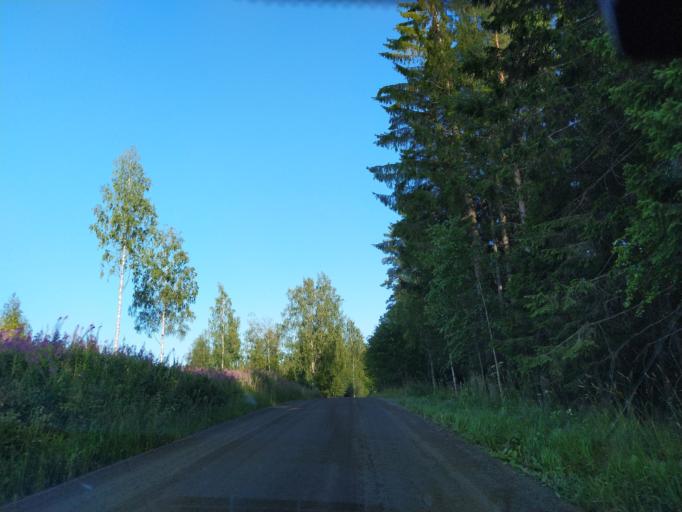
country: FI
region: Central Finland
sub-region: Jaemsae
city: Kuhmoinen
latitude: 61.6040
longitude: 25.1422
